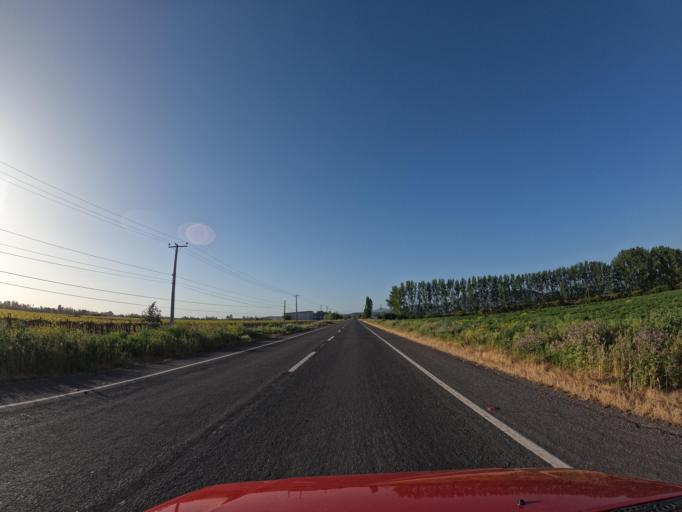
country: CL
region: O'Higgins
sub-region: Provincia de Colchagua
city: Santa Cruz
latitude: -34.4589
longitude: -71.3641
